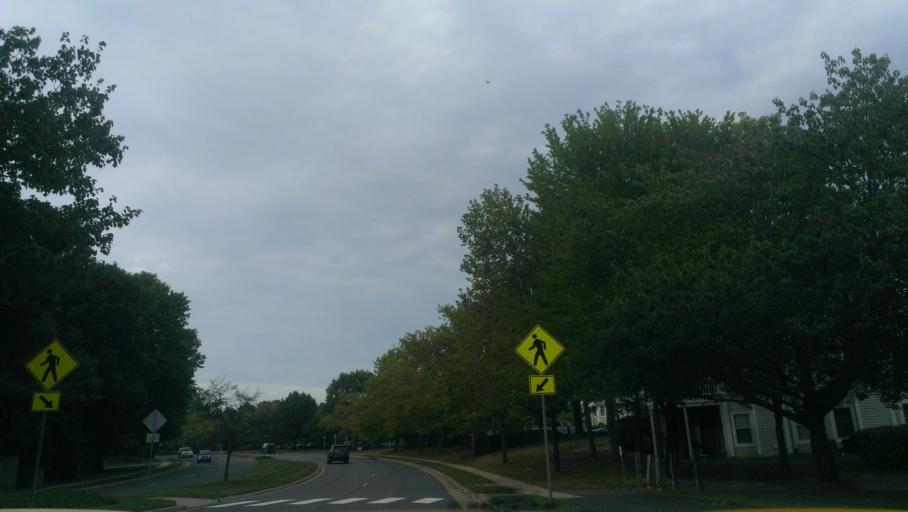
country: US
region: Virginia
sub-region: Fairfax County
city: Merrifield
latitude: 38.8728
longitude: -77.2163
